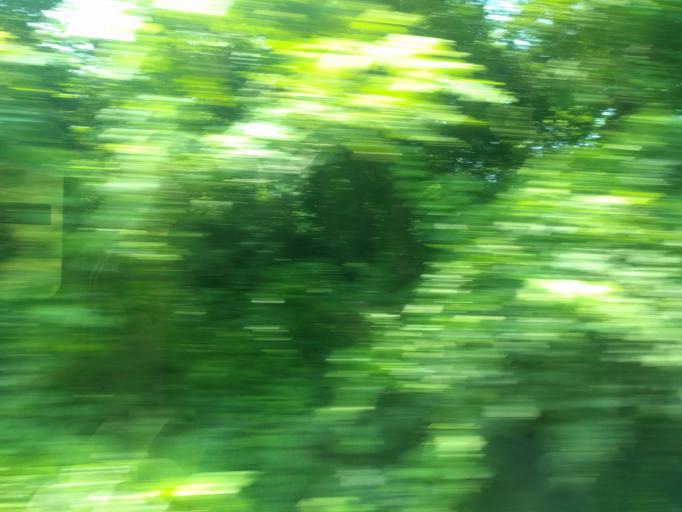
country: JP
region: Fukushima
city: Inawashiro
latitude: 37.4941
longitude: 140.2312
